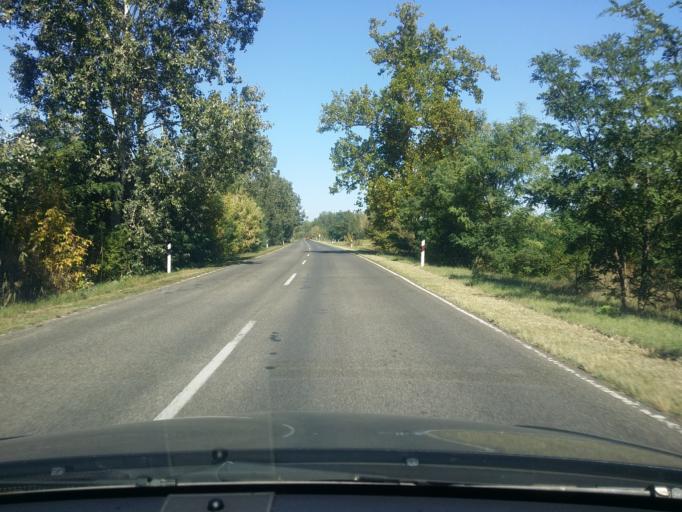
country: HU
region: Csongrad
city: Kistelek
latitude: 46.5127
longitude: 19.9679
